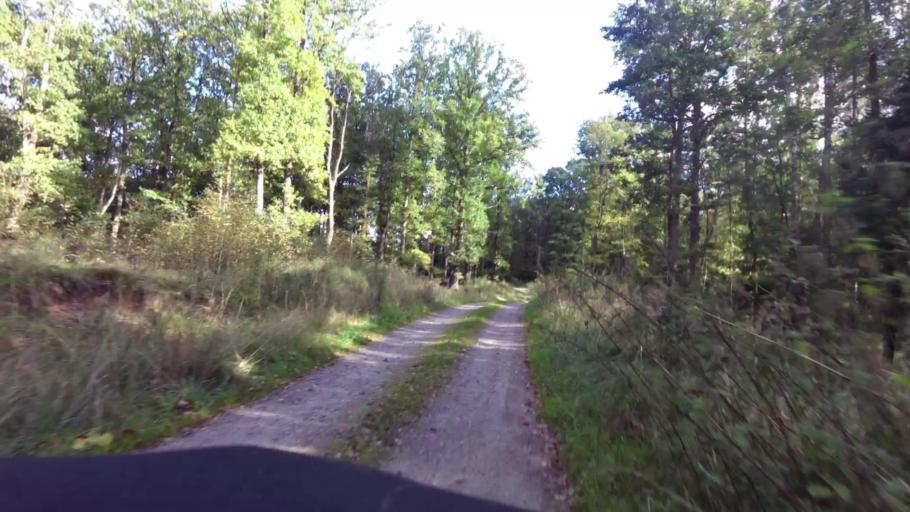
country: PL
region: West Pomeranian Voivodeship
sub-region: Powiat bialogardzki
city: Bialogard
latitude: 54.0401
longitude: 16.1336
